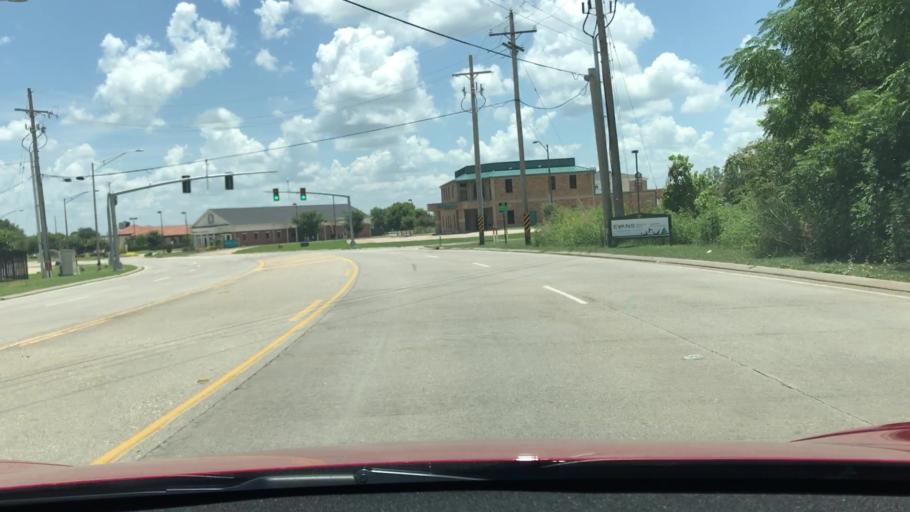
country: US
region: Louisiana
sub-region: Bossier Parish
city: Bossier City
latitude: 32.4266
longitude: -93.7248
